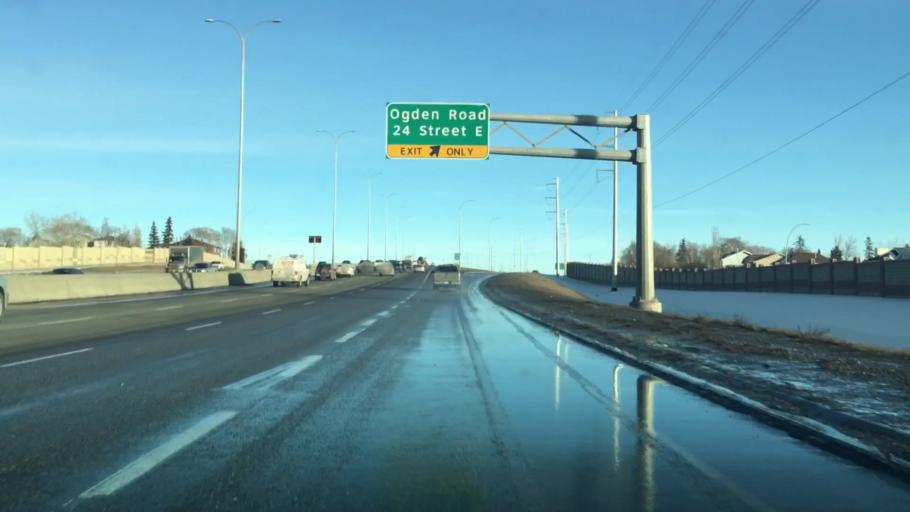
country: CA
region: Alberta
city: Calgary
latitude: 50.9791
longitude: -114.0054
